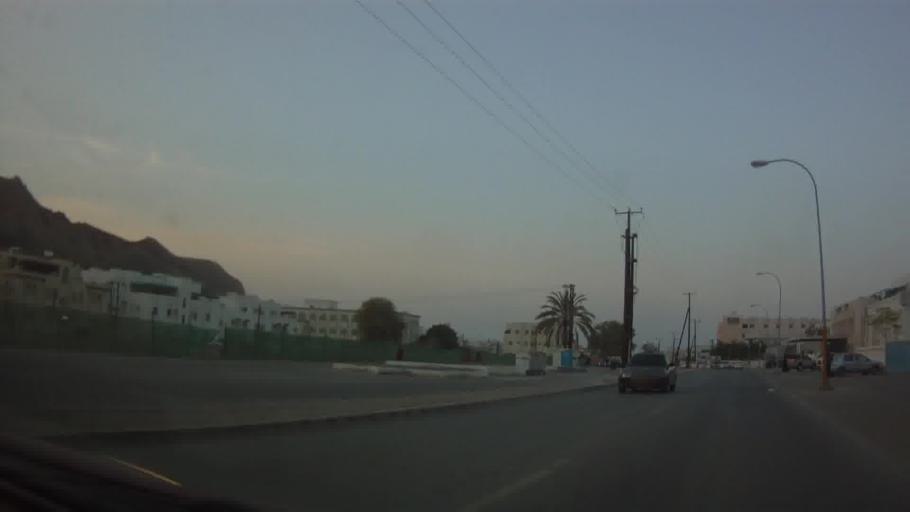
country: OM
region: Muhafazat Masqat
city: Muscat
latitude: 23.6263
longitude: 58.5414
